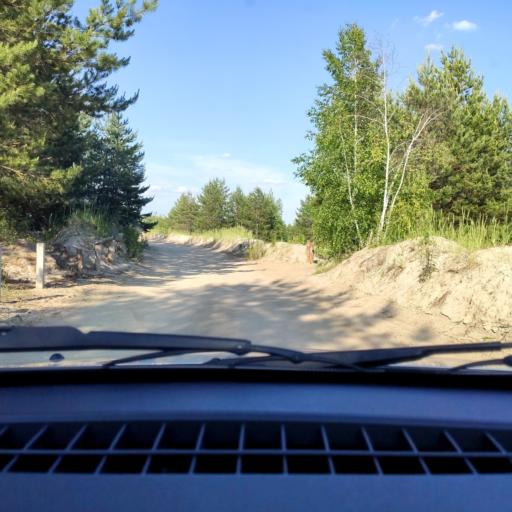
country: RU
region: Voronezj
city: Somovo
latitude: 51.7769
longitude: 39.2894
